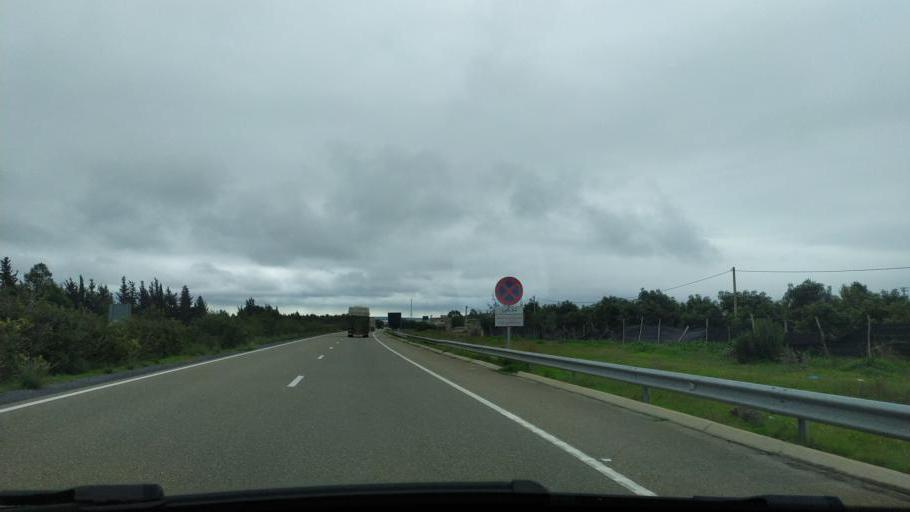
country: MA
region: Gharb-Chrarda-Beni Hssen
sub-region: Kenitra Province
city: Lalla Mimouna
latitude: 34.8842
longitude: -6.2110
